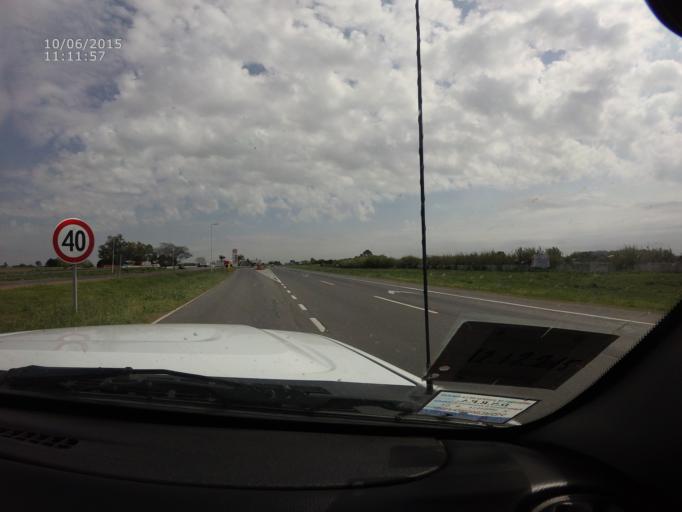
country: AR
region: Santa Fe
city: Arroyo Seco
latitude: -33.1358
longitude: -60.5695
